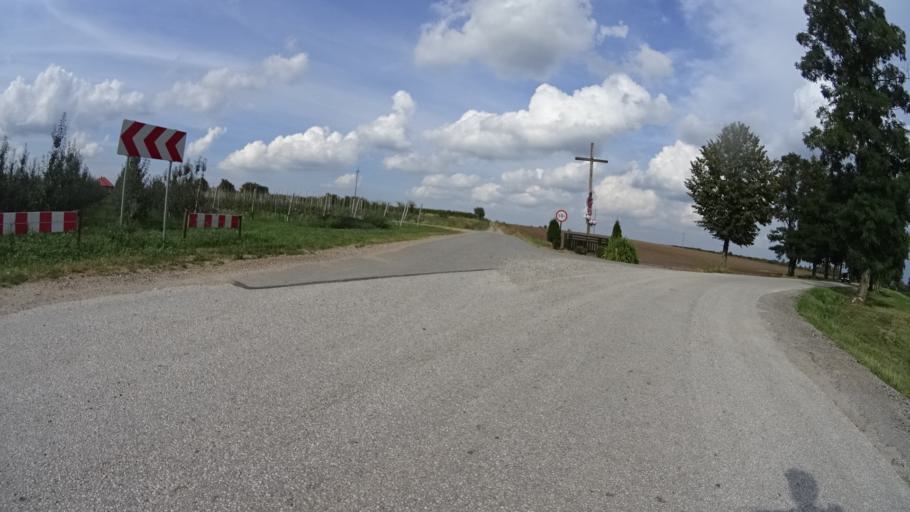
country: PL
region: Masovian Voivodeship
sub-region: Powiat grojecki
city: Goszczyn
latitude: 51.6950
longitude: 20.8216
